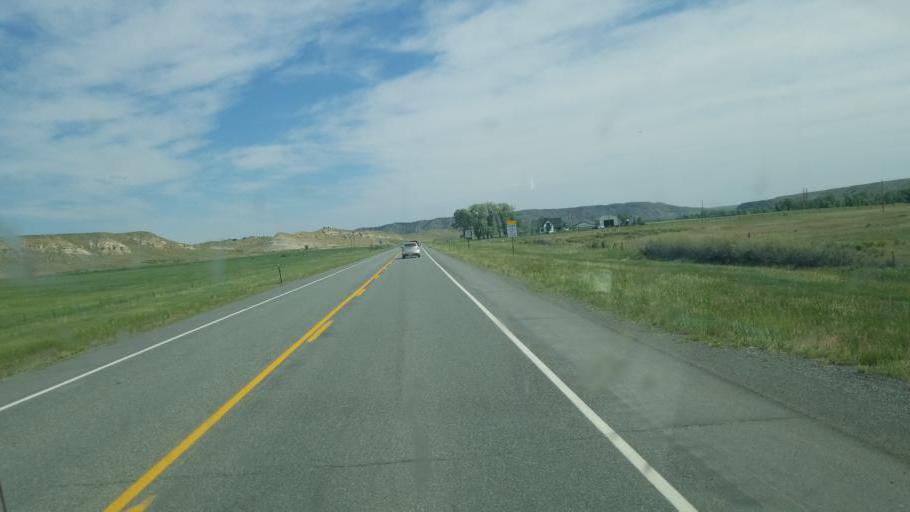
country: US
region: Wyoming
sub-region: Park County
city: Cody
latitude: 44.1634
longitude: -108.8761
